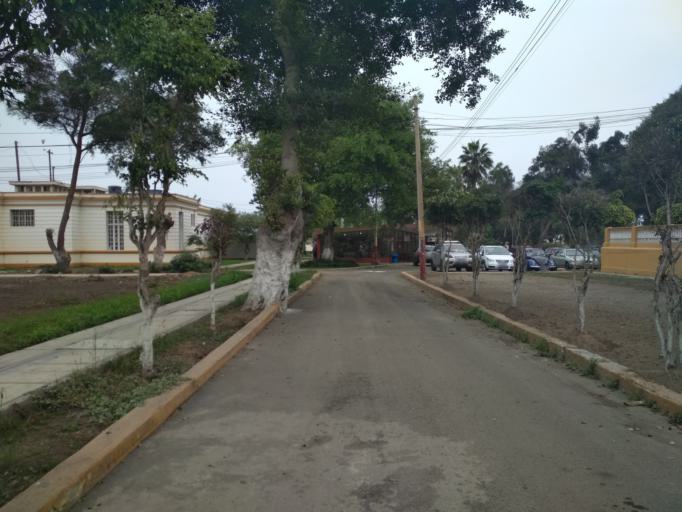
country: PE
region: Lima
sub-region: Lima
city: San Isidro
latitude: -12.0981
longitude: -77.0650
